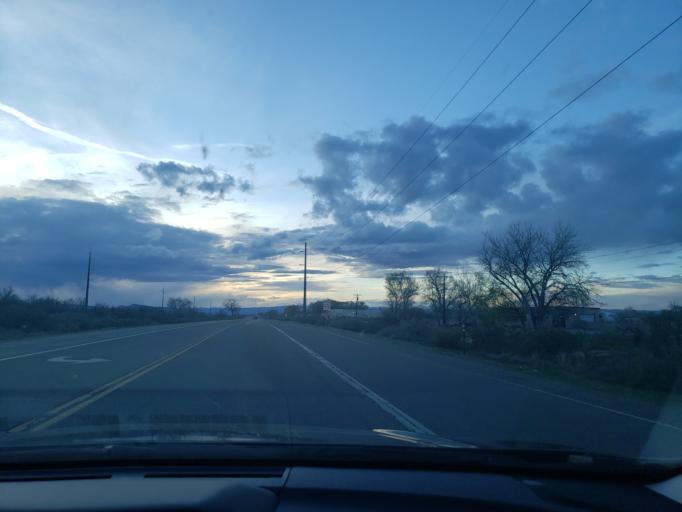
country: US
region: Colorado
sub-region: Mesa County
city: Fruita
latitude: 39.1392
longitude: -108.7015
